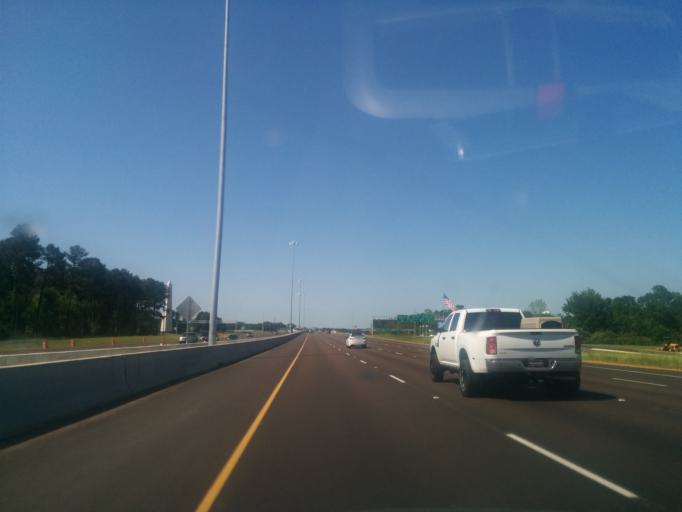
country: US
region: Mississippi
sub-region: Madison County
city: Ridgeland
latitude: 32.4410
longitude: -90.1444
